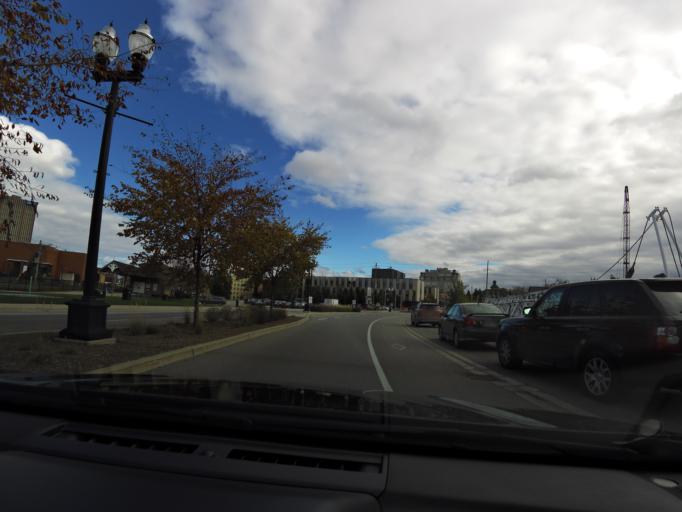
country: CA
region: Ontario
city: Waterloo
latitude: 43.4645
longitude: -80.5278
